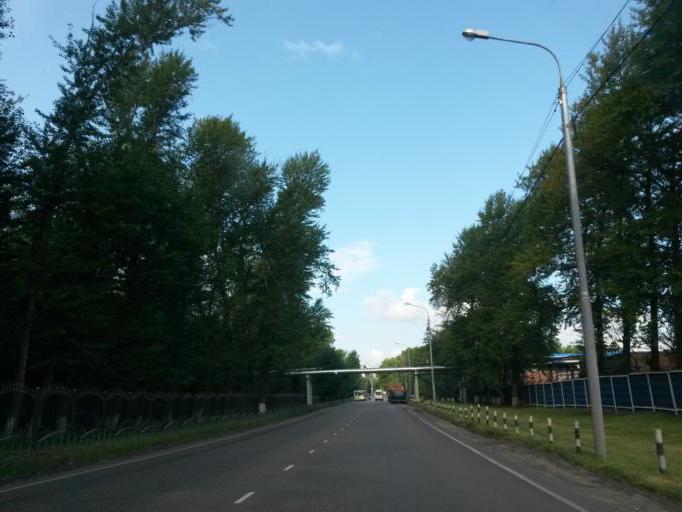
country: RU
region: Moscow
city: Kapotnya
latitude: 55.6412
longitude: 37.8047
